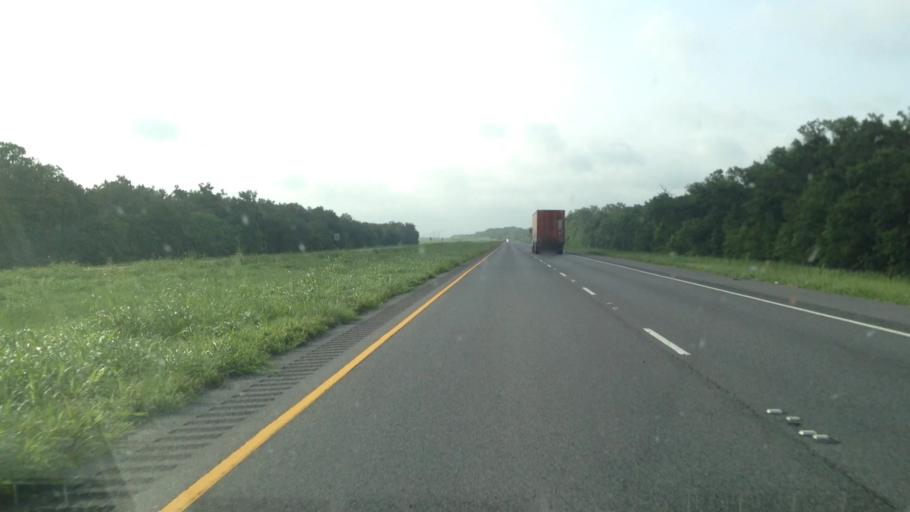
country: US
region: Louisiana
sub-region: Evangeline Parish
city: Ville Platte
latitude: 30.7331
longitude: -92.1316
